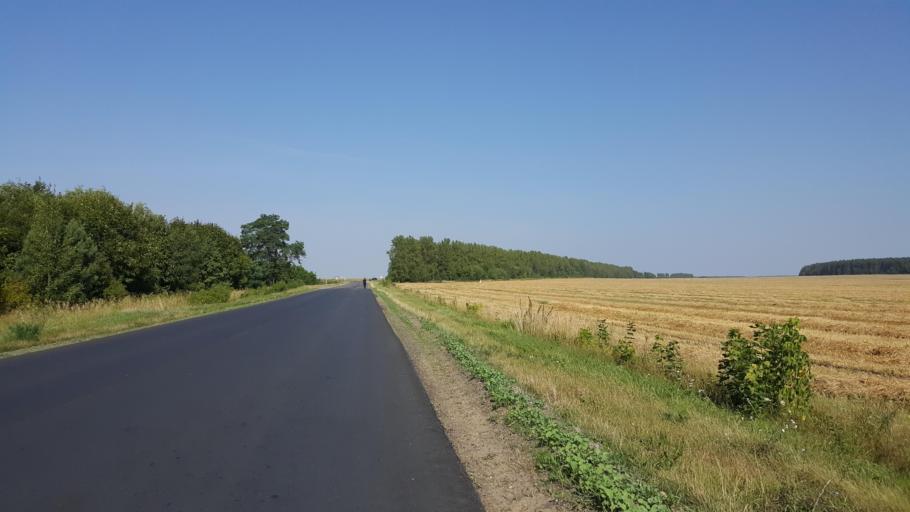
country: BY
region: Brest
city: Kamyanyets
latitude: 52.4420
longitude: 23.7419
